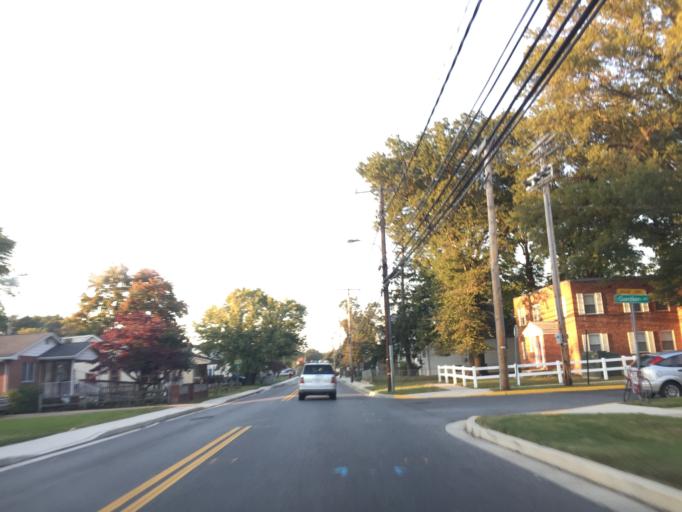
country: US
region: Maryland
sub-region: Baltimore County
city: Essex
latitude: 39.3089
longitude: -76.4644
